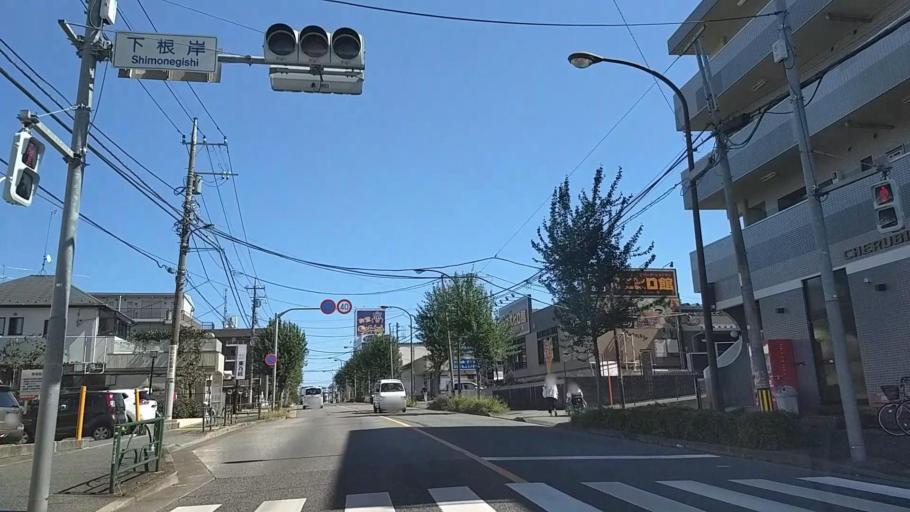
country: JP
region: Tokyo
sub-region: Machida-shi
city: Machida
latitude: 35.5761
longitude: 139.4155
